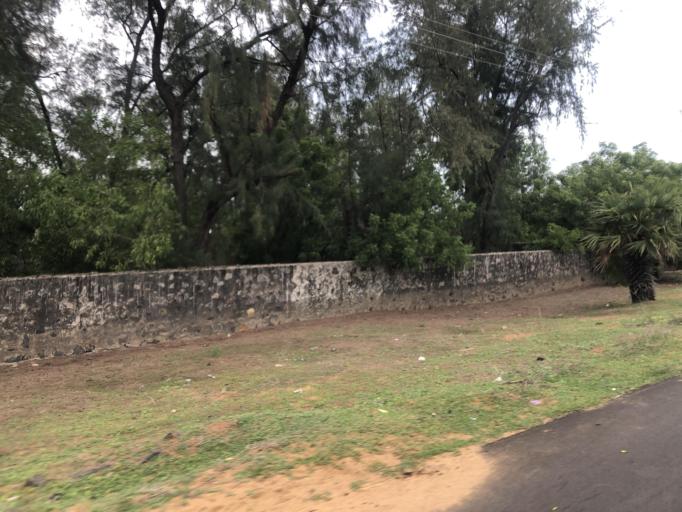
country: IN
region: Tamil Nadu
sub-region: Kancheepuram
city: Mamallapuram
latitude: 12.6023
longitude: 80.1878
